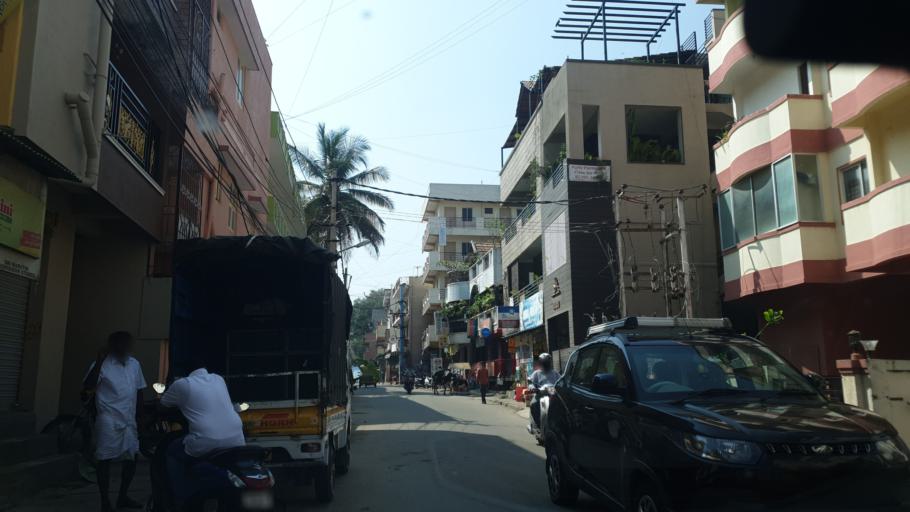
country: IN
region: Karnataka
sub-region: Bangalore Urban
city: Bangalore
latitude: 12.9768
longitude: 77.6661
